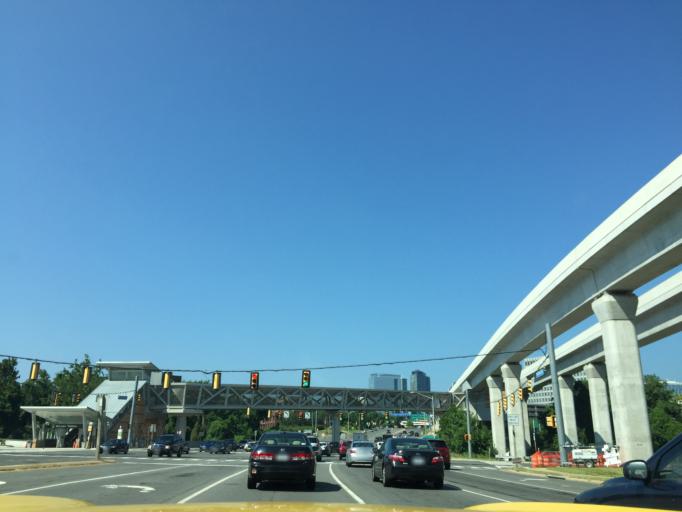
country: US
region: Virginia
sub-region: Fairfax County
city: Pimmit Hills
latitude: 38.9254
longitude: -77.2077
